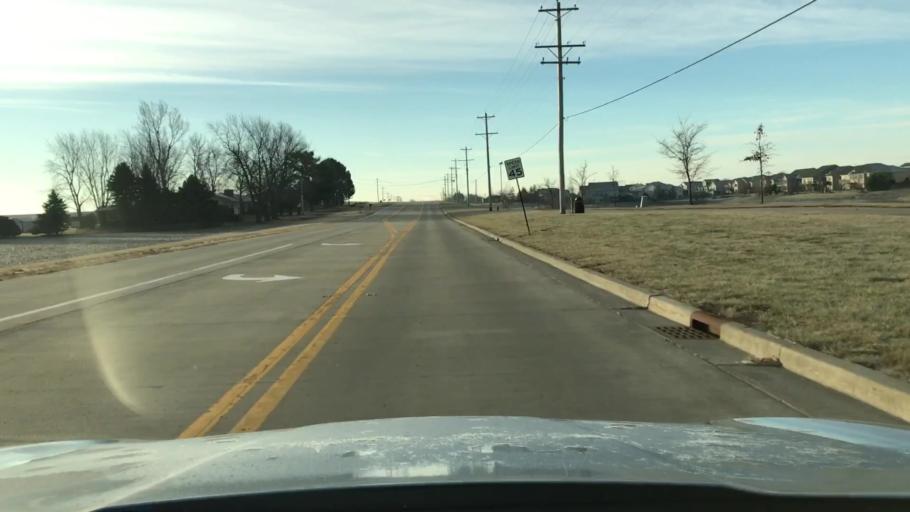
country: US
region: Illinois
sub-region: McLean County
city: Normal
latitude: 40.5567
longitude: -88.9446
